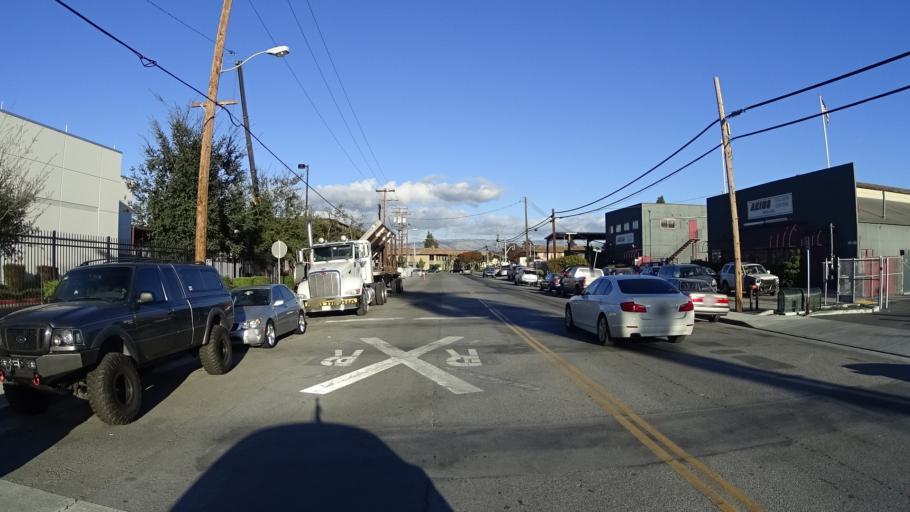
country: US
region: California
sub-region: Santa Clara County
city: Santa Clara
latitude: 37.3601
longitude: -121.9431
